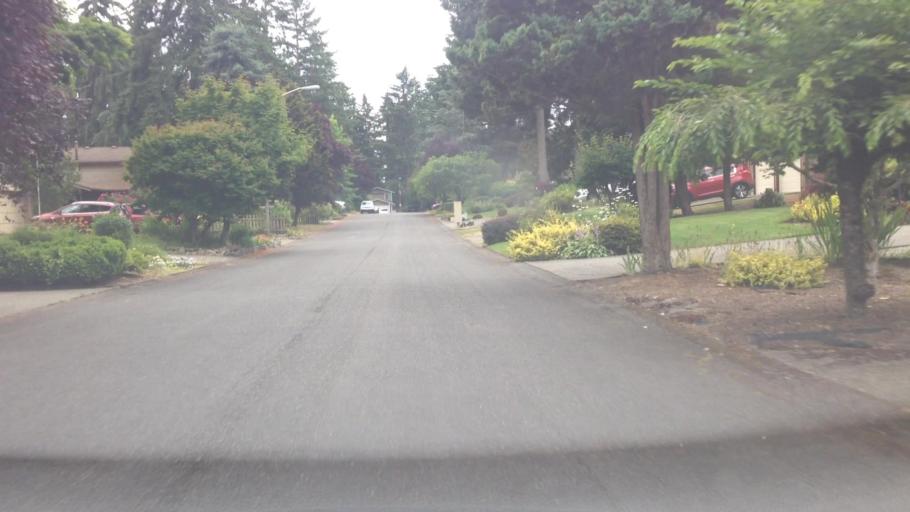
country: US
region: Washington
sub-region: Pierce County
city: South Hill
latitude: 47.1091
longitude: -122.2995
